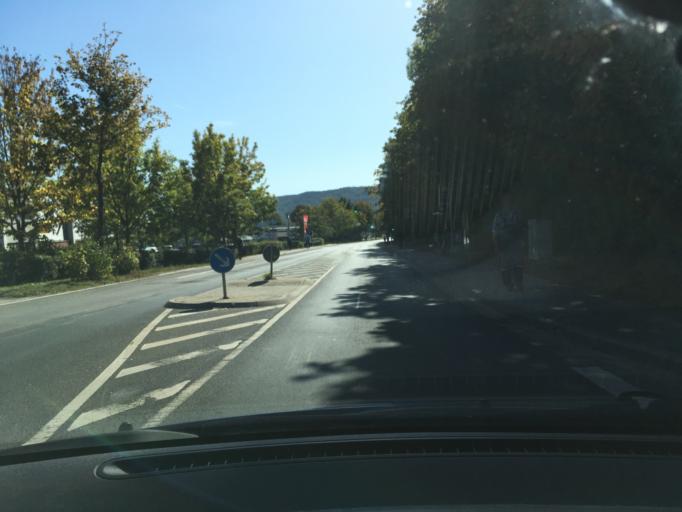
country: DE
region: Lower Saxony
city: Springe
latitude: 52.2130
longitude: 9.5681
